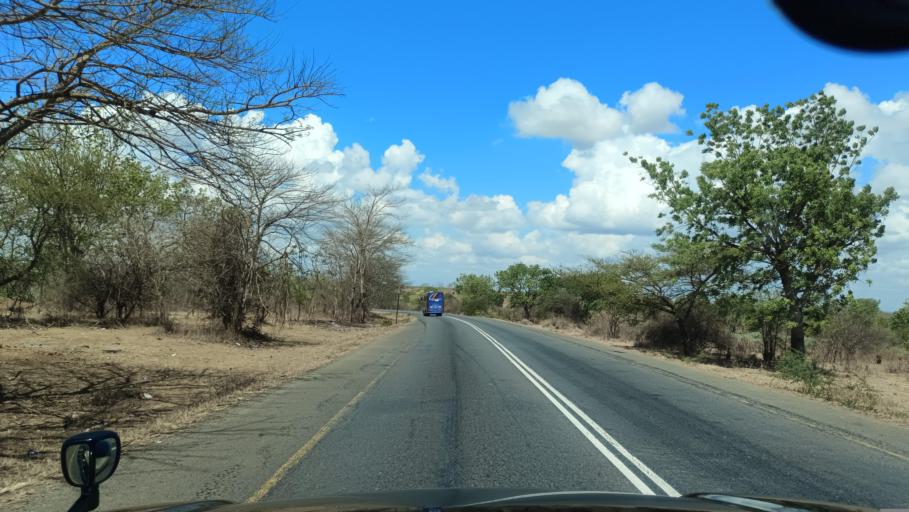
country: TZ
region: Morogoro
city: Morogoro
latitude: -6.9055
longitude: 37.4791
